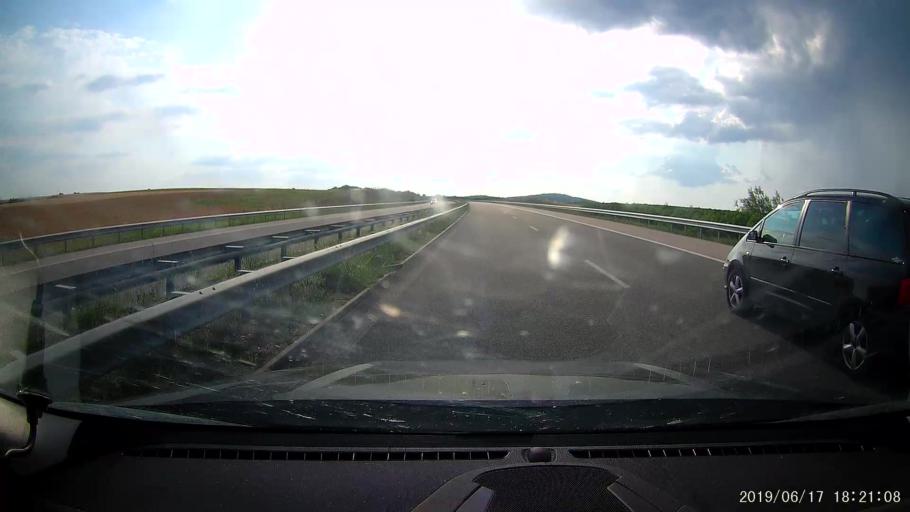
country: BG
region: Khaskovo
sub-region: Obshtina Simeonovgrad
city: Simeonovgrad
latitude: 41.9669
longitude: 25.7925
